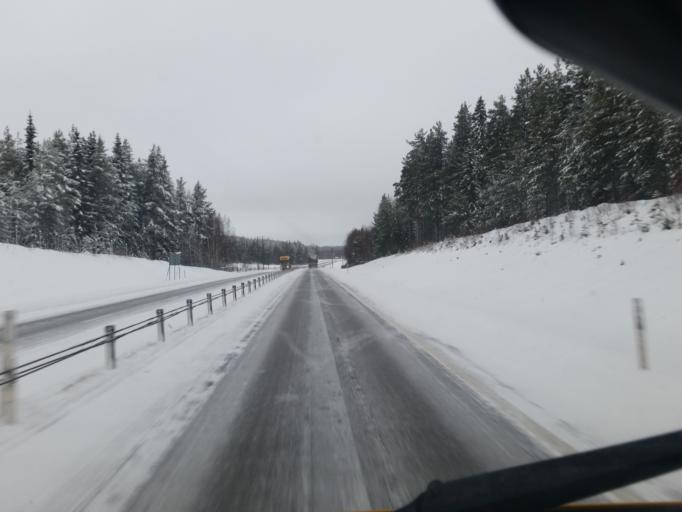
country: SE
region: Norrbotten
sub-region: Pitea Kommun
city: Pitea
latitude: 65.2499
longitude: 21.4804
